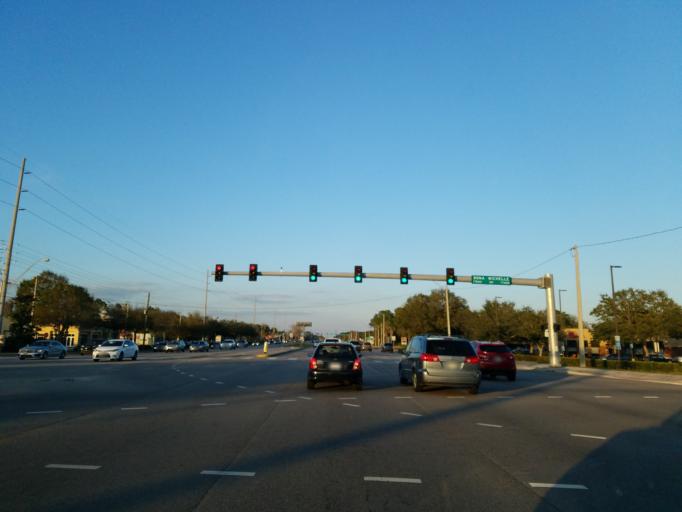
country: US
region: Florida
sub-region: Hillsborough County
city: Pebble Creek
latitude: 28.1268
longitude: -82.3692
